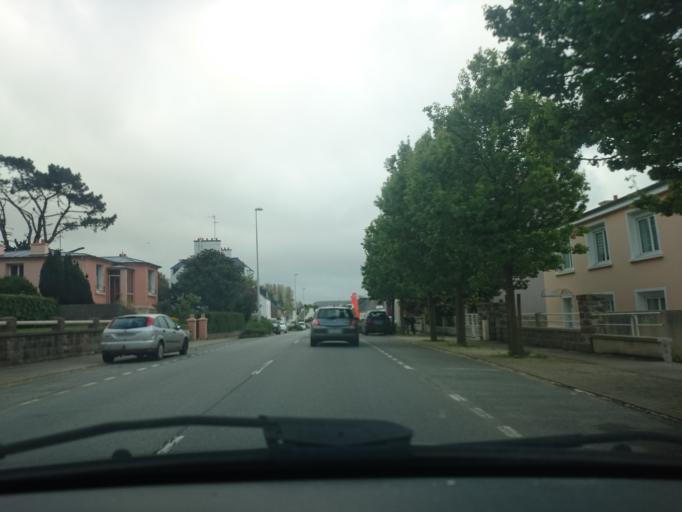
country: FR
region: Brittany
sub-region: Departement du Finistere
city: Saint-Renan
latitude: 48.4369
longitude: -4.6192
